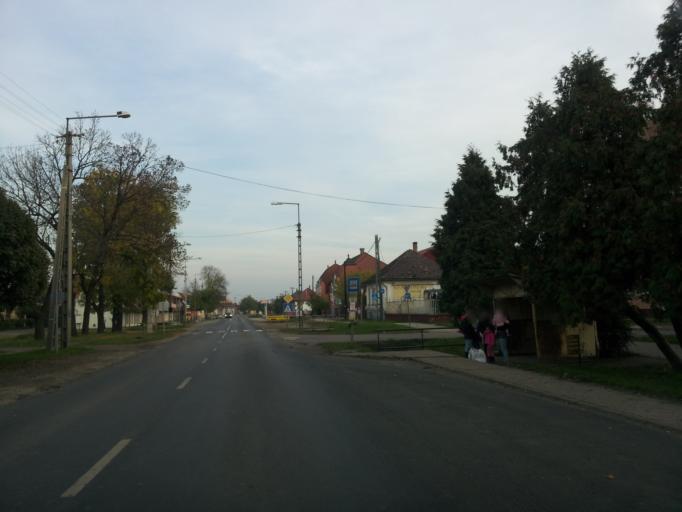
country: HU
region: Pest
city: Nagykata
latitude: 47.4183
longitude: 19.7441
